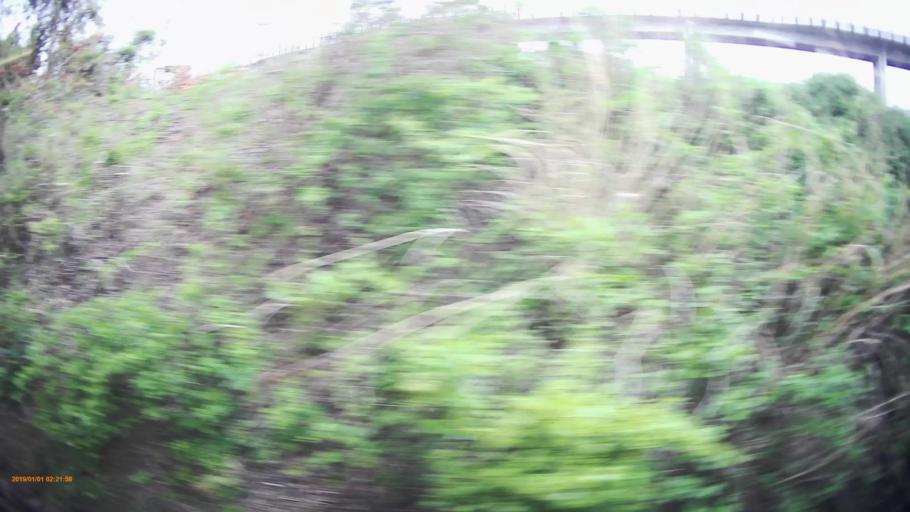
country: JP
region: Yamanashi
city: Ryuo
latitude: 35.6826
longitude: 138.4944
